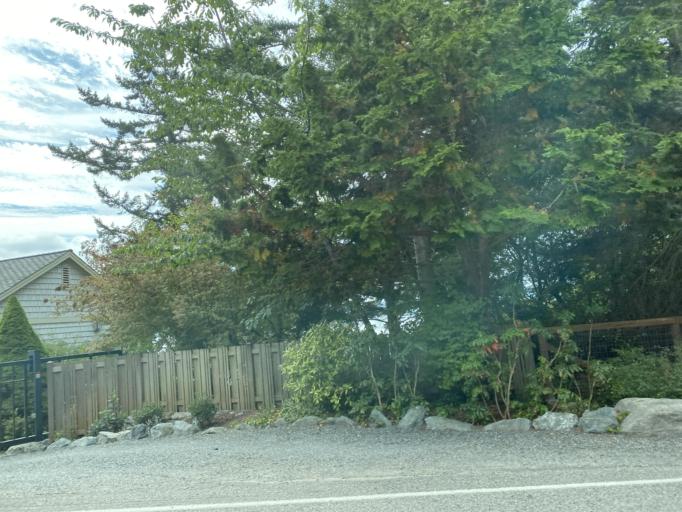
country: US
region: Washington
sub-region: Island County
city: Coupeville
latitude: 48.2394
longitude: -122.6966
